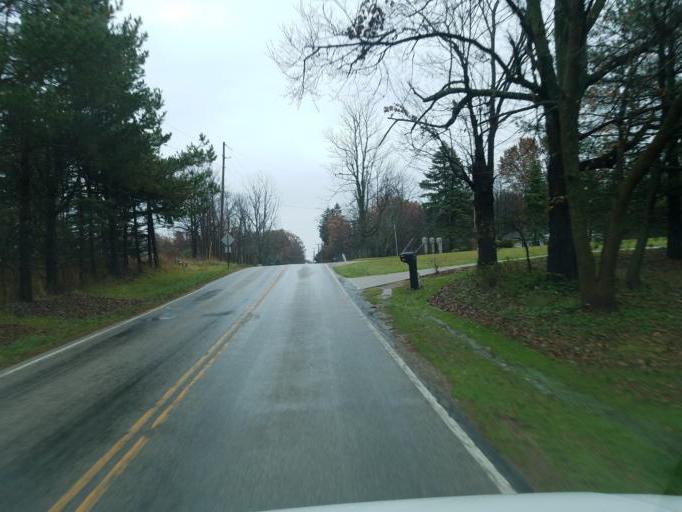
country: US
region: Ohio
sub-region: Richland County
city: Ontario
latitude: 40.7469
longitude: -82.5989
